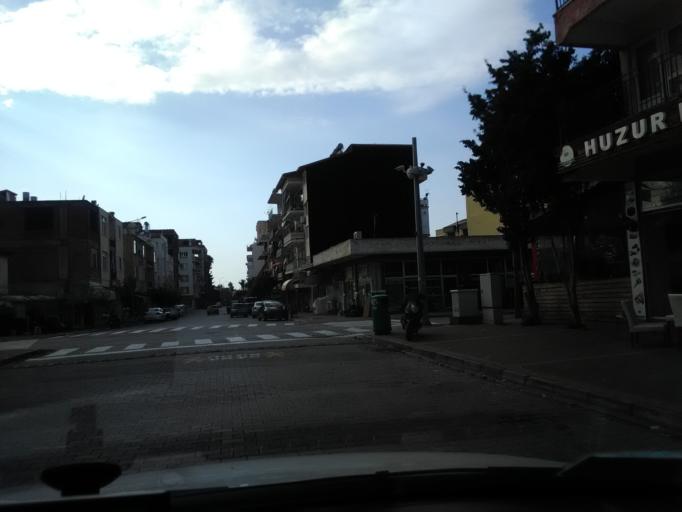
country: TR
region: Antalya
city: Gazipasa
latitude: 36.2690
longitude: 32.3219
